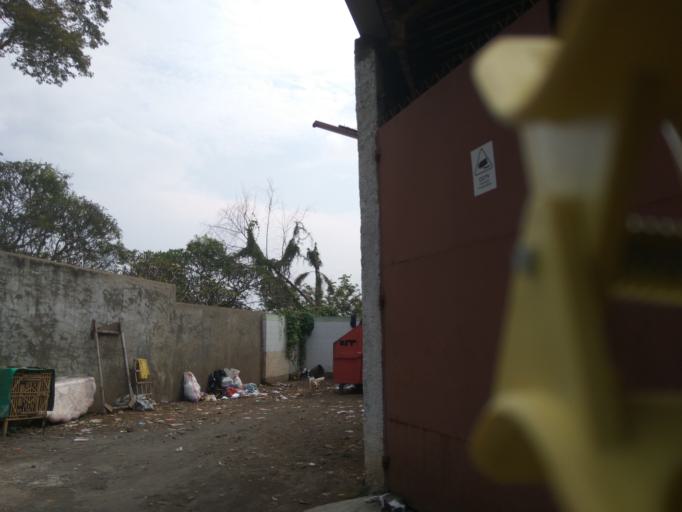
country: ID
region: Central Java
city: Semarang
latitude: -7.0445
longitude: 110.4159
